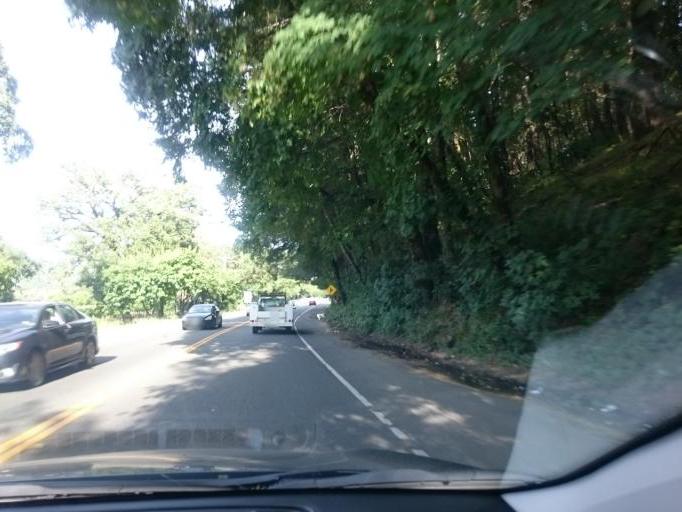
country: US
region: California
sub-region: Napa County
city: Calistoga
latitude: 38.5742
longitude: -122.5771
